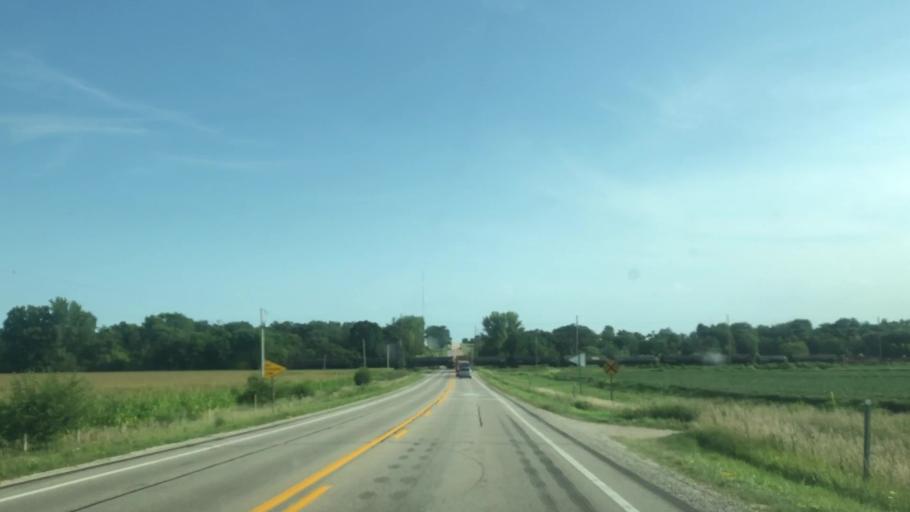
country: US
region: Iowa
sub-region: Marshall County
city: Marshalltown
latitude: 42.0321
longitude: -93.0001
